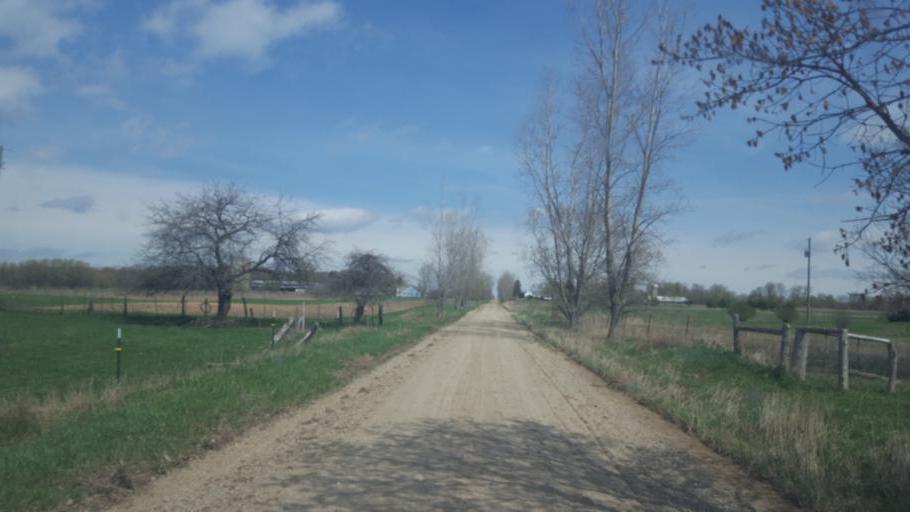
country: US
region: Michigan
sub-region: Montcalm County
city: Edmore
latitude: 43.4843
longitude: -84.9459
